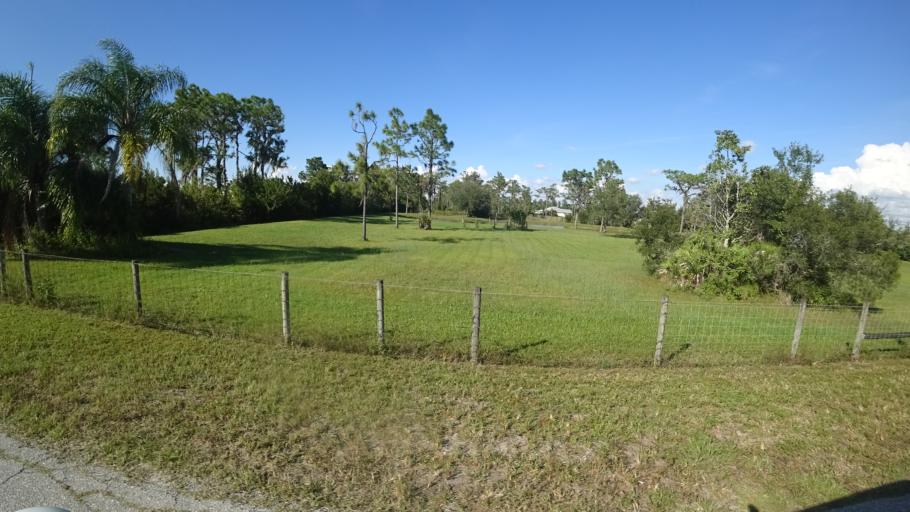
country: US
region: Florida
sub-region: Sarasota County
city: Fruitville
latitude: 27.4015
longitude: -82.2852
